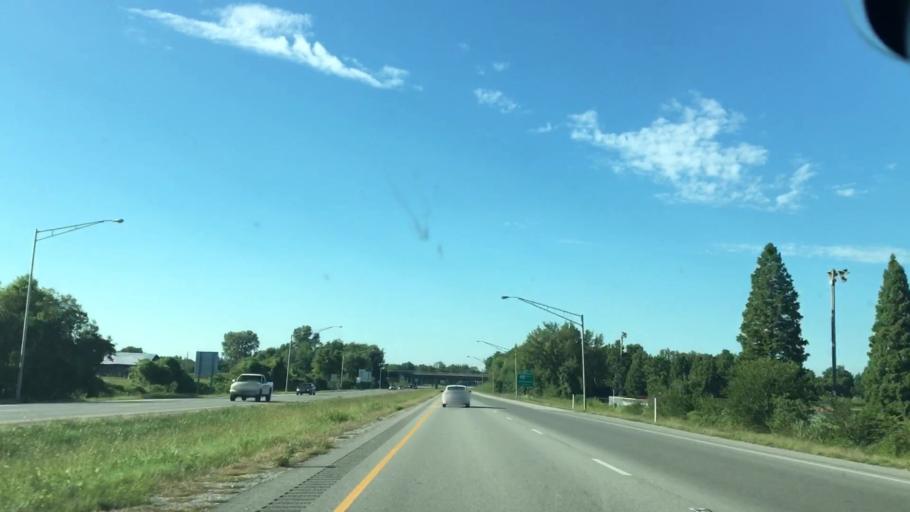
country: US
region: Kentucky
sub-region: Daviess County
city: Owensboro
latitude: 37.7603
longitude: -87.1609
